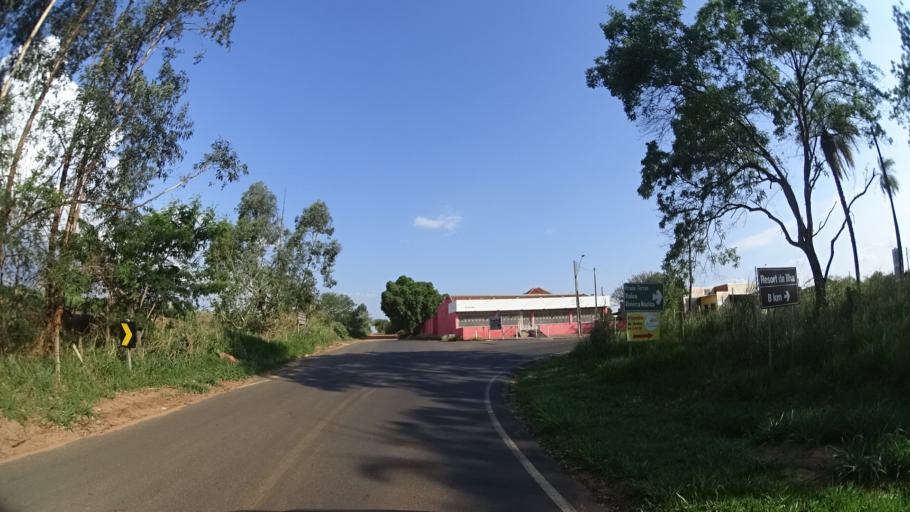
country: BR
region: Sao Paulo
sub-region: Urupes
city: Urupes
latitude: -21.3704
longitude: -49.4714
